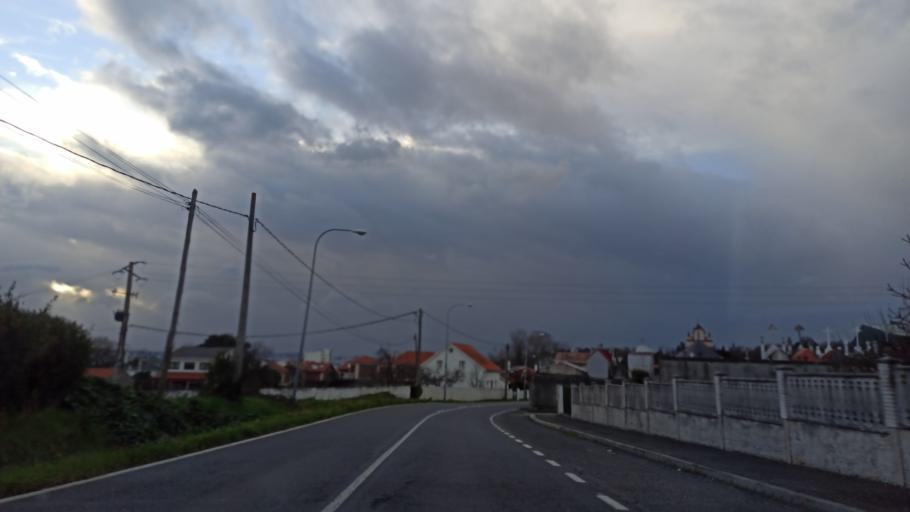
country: ES
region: Galicia
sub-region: Provincia da Coruna
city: Oleiros
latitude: 43.3821
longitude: -8.3302
